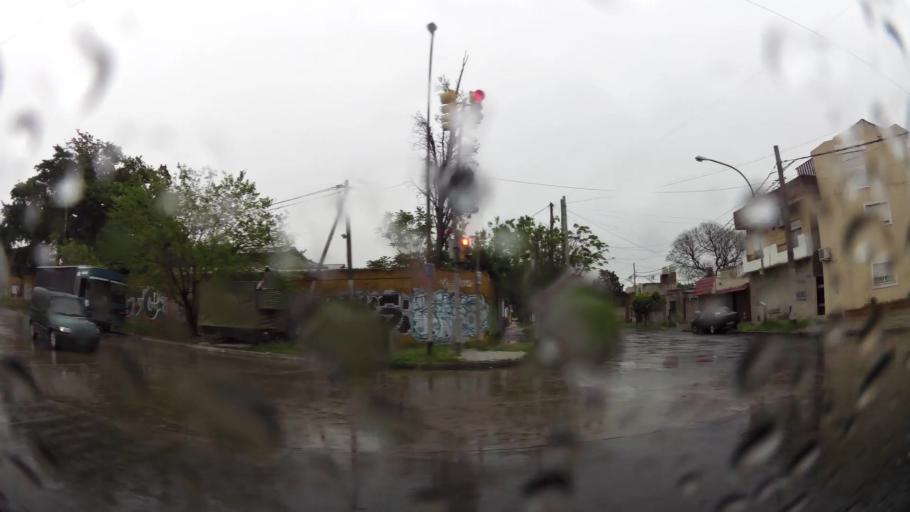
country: AR
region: Buenos Aires
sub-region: Partido de Lanus
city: Lanus
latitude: -34.7012
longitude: -58.4128
